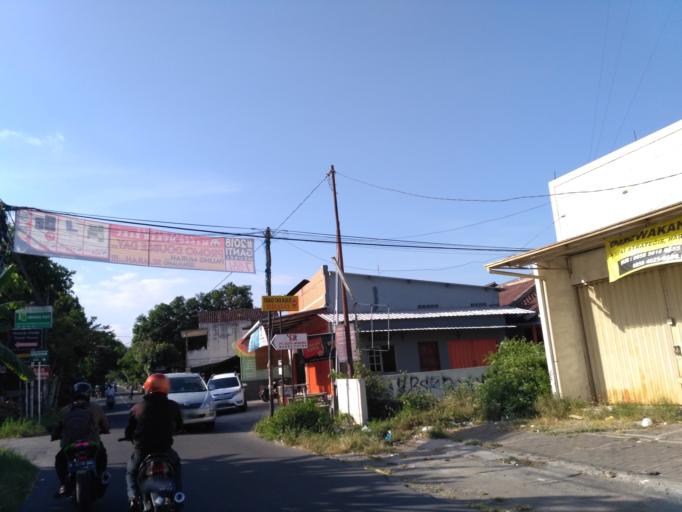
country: ID
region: Daerah Istimewa Yogyakarta
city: Depok
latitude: -7.7811
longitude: 110.4228
